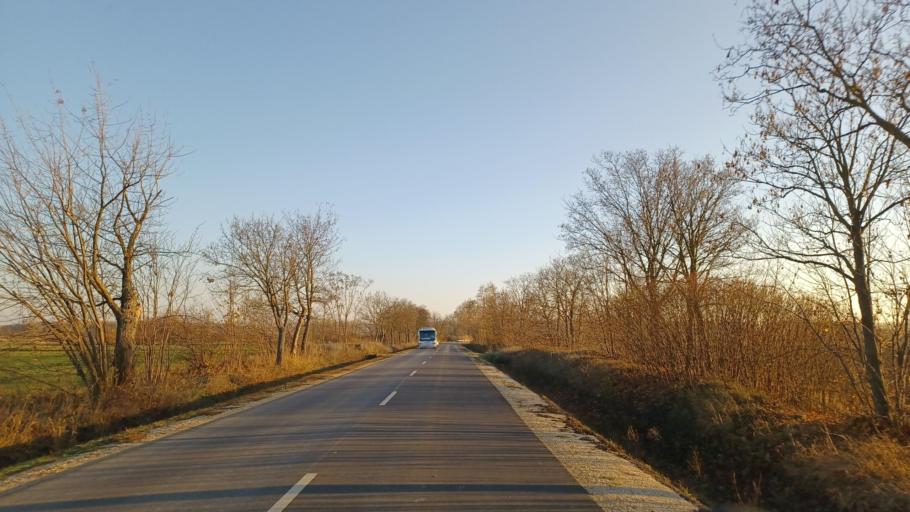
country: HU
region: Tolna
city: Fadd
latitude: 46.4896
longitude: 18.8360
